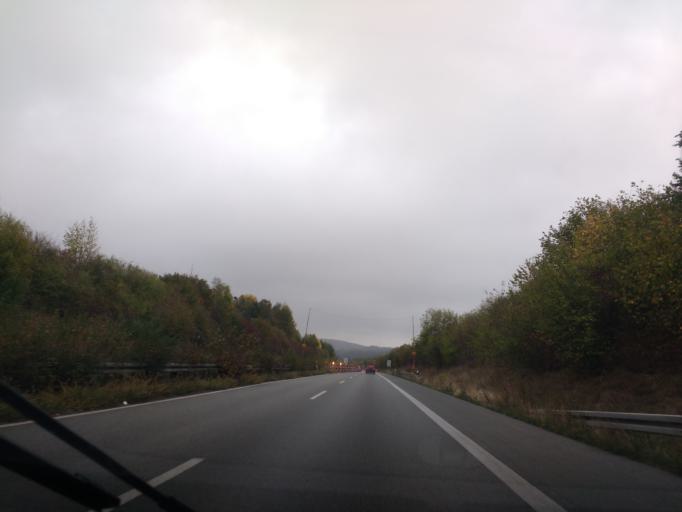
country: DE
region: Lower Saxony
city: Hilter
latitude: 52.1861
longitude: 8.1480
